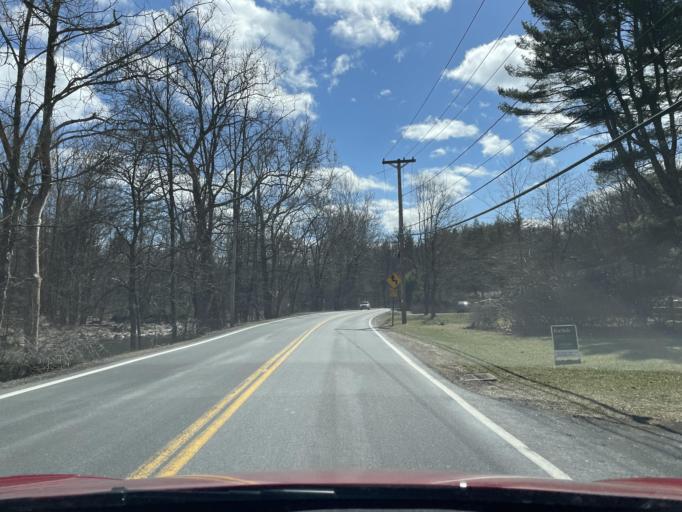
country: US
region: New York
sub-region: Ulster County
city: Zena
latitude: 42.0310
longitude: -74.0835
